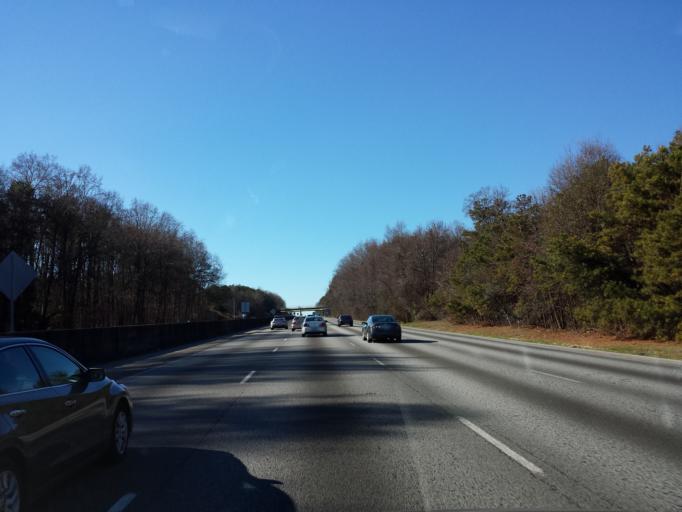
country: US
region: Georgia
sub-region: Cobb County
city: Mableton
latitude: 33.7748
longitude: -84.5721
